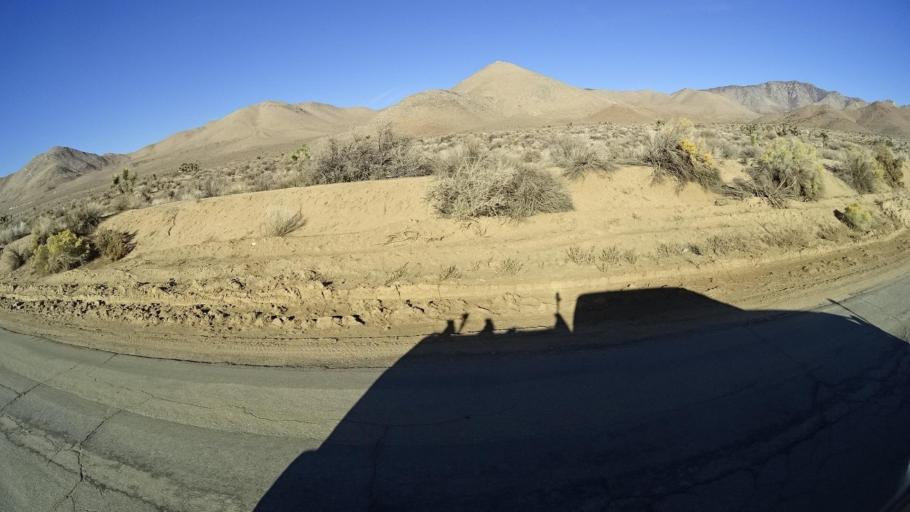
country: US
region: California
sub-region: Kern County
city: Weldon
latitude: 35.5507
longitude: -118.2117
